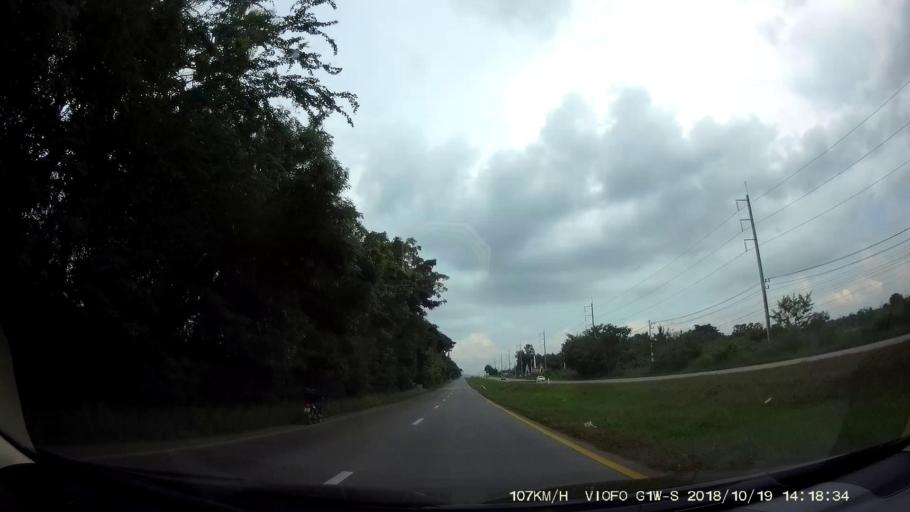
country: TH
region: Chaiyaphum
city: Kaeng Khro
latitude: 16.0172
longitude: 102.2365
